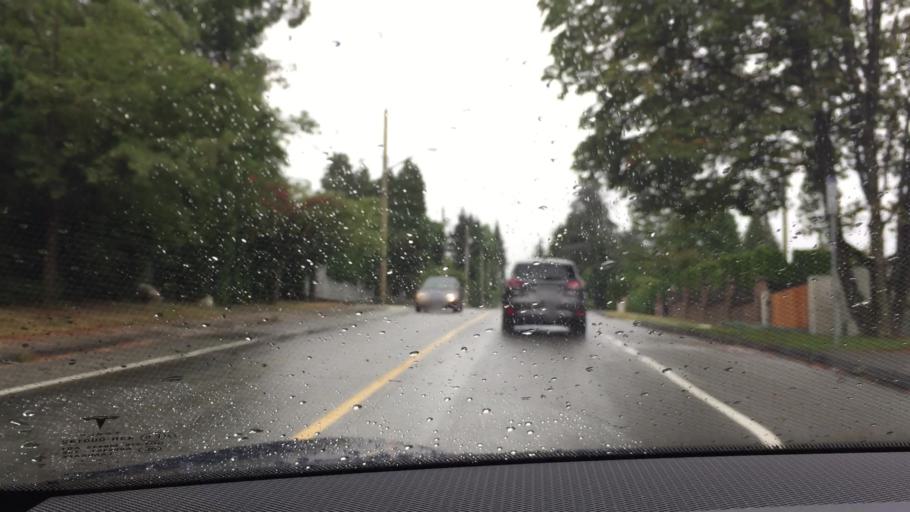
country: CA
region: British Columbia
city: Burnaby
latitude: 49.2325
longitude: -122.9599
